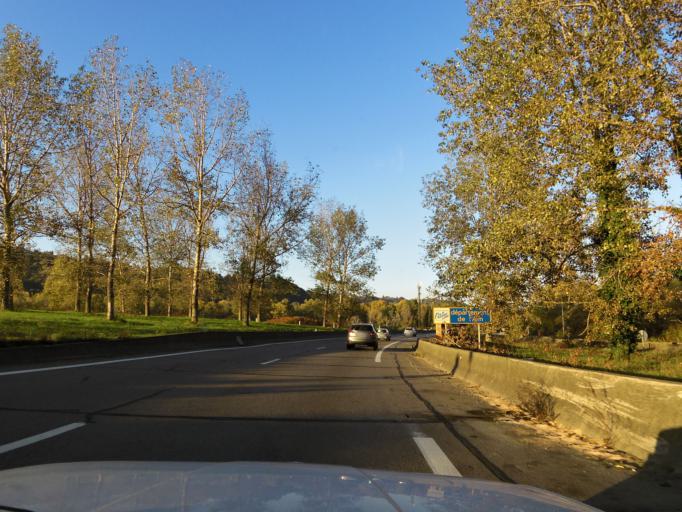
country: FR
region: Rhone-Alpes
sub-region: Departement du Rhone
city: Vaulx-en-Velin
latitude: 45.8046
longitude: 4.9261
